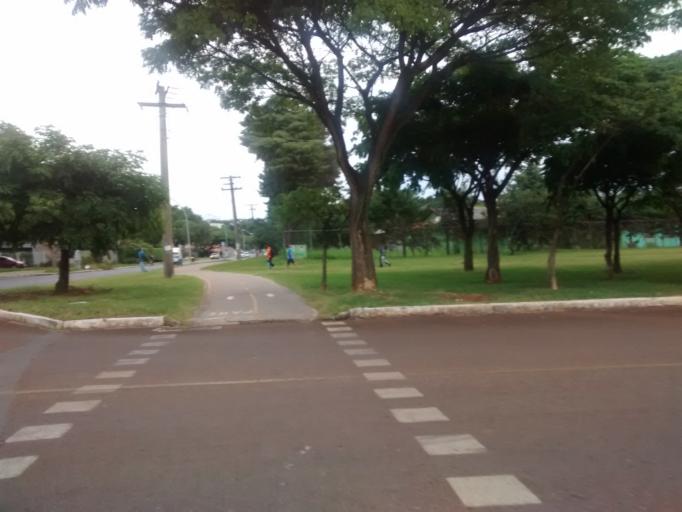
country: BR
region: Federal District
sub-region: Brasilia
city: Brasilia
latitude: -15.7517
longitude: -47.8981
